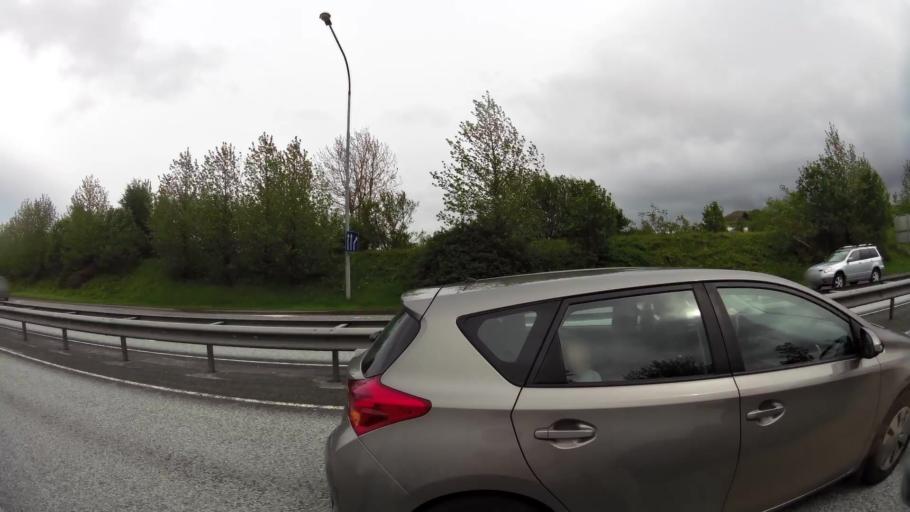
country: IS
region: Capital Region
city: Hafnarfjoerdur
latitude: 64.0727
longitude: -21.9393
